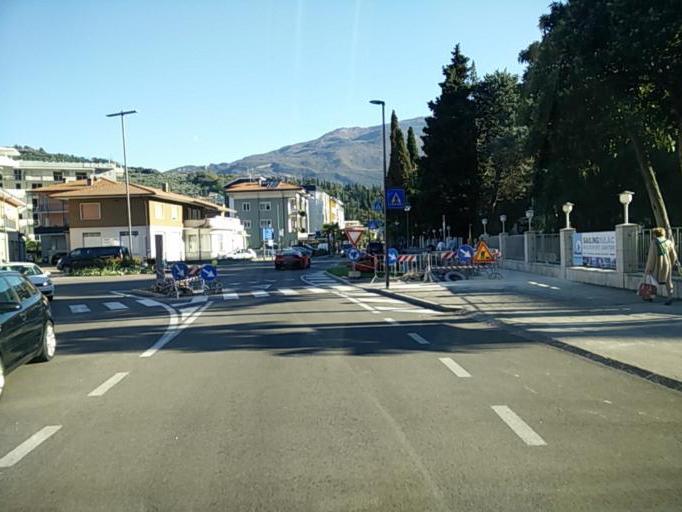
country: IT
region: Trentino-Alto Adige
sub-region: Provincia di Trento
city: Riva del Garda
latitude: 45.8825
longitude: 10.8536
